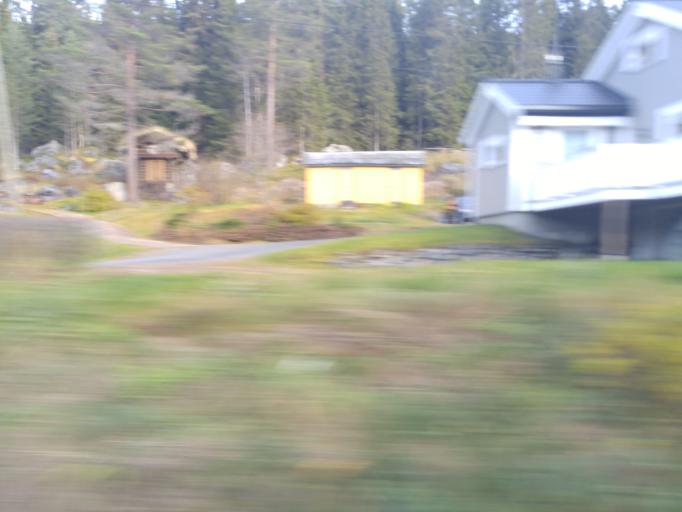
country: NO
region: Oppland
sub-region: Nord-Aurdal
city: Fagernes
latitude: 61.0376
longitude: 9.1754
